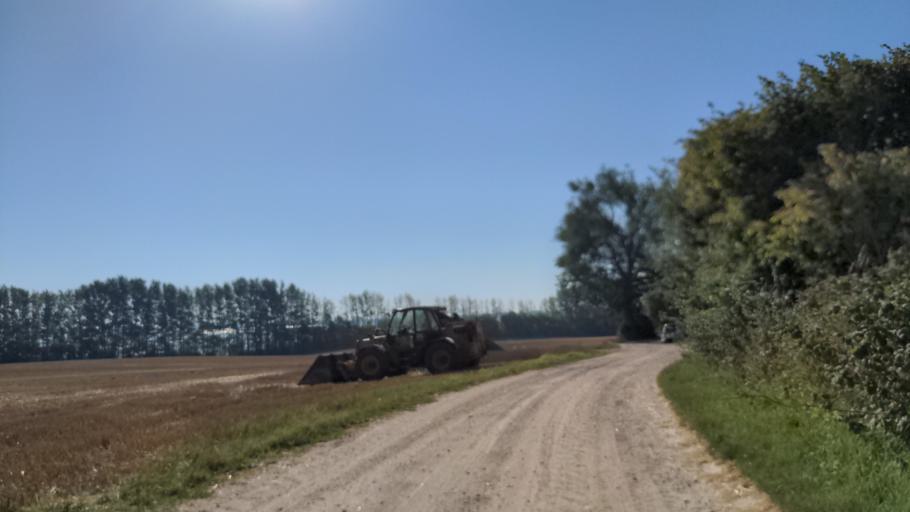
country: DE
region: Mecklenburg-Vorpommern
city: Ostseebad Boltenhagen
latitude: 53.9581
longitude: 11.2375
